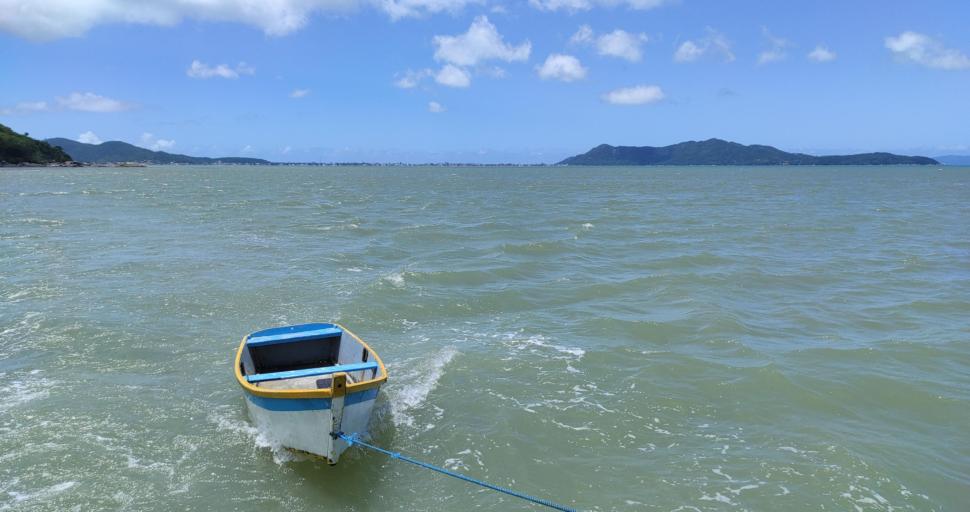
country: BR
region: Santa Catarina
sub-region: Porto Belo
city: Porto Belo
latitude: -27.2010
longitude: -48.5618
